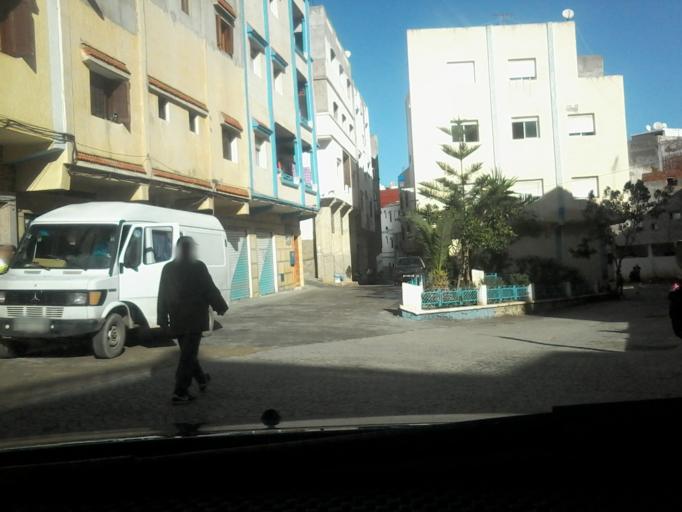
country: MA
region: Tanger-Tetouan
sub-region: Tetouan
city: Martil
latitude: 35.6793
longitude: -5.3271
